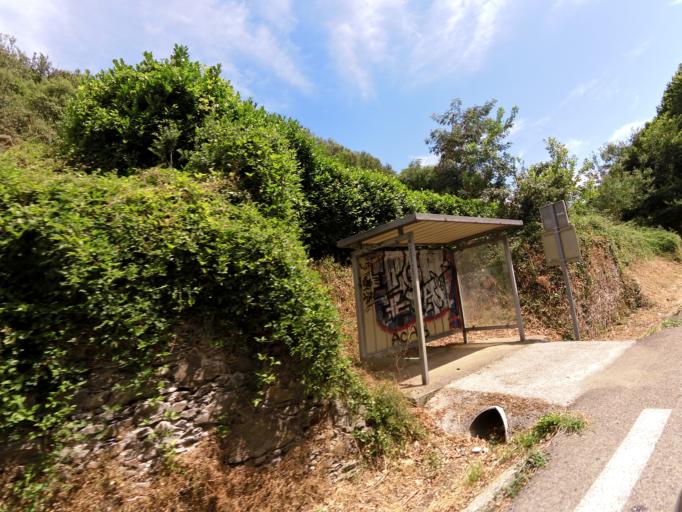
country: FR
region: Languedoc-Roussillon
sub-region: Departement du Gard
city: Sumene
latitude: 43.9929
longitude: 3.6780
